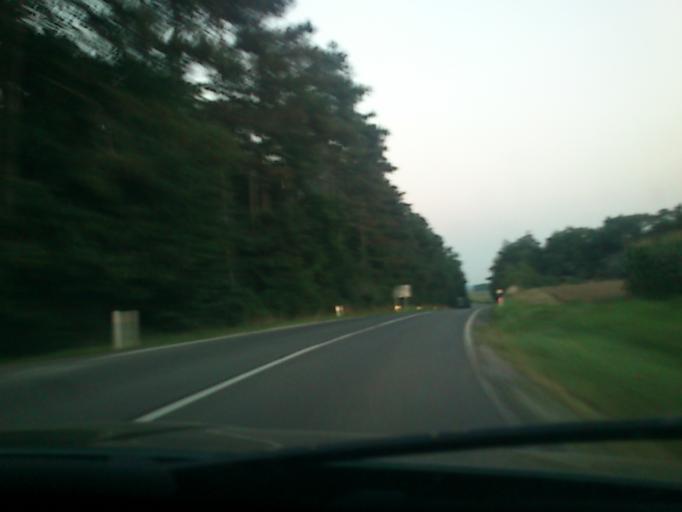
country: SI
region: Duplek
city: Zgornji Duplek
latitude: 46.4952
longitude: 15.7155
